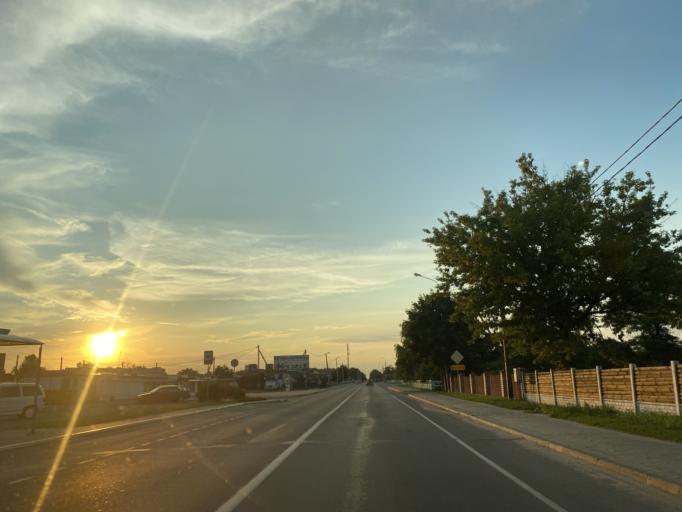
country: BY
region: Brest
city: Ivatsevichy
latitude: 52.7088
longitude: 25.3545
